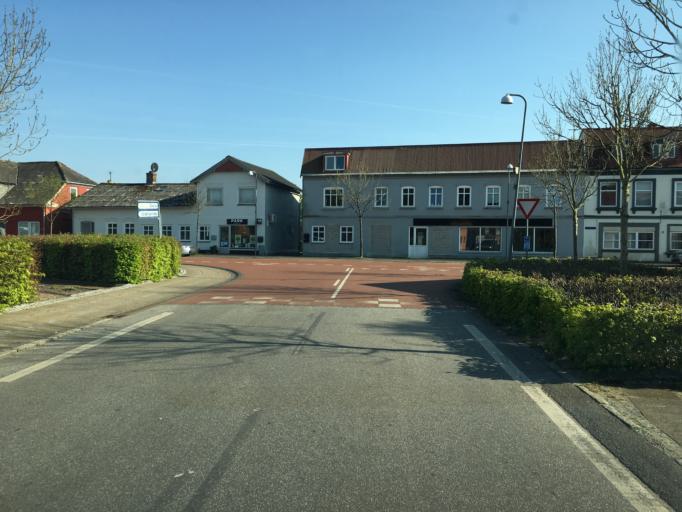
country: DK
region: South Denmark
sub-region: Aabenraa Kommune
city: Rodekro
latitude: 55.0757
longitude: 9.2122
